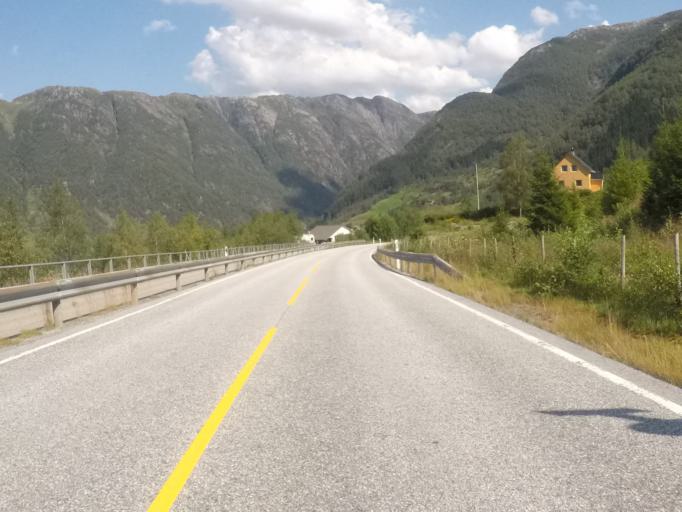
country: NO
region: Hordaland
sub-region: Masfjorden
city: Masfjorden
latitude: 60.8998
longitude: 5.5217
